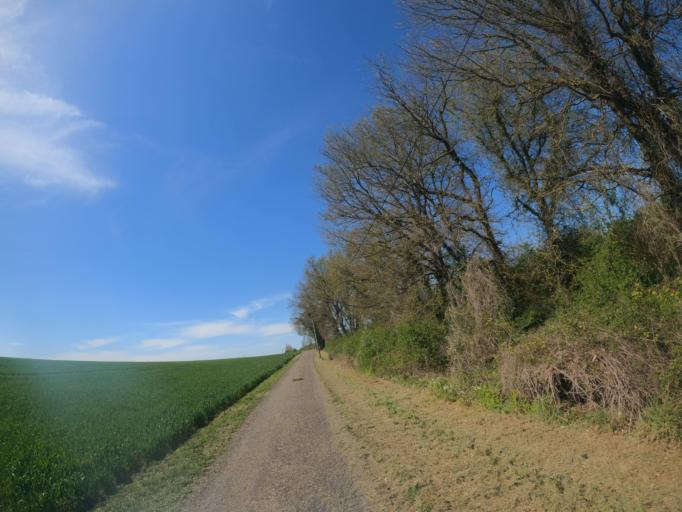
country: FR
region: Poitou-Charentes
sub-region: Departement des Deux-Sevres
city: Airvault
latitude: 46.8841
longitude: -0.1498
